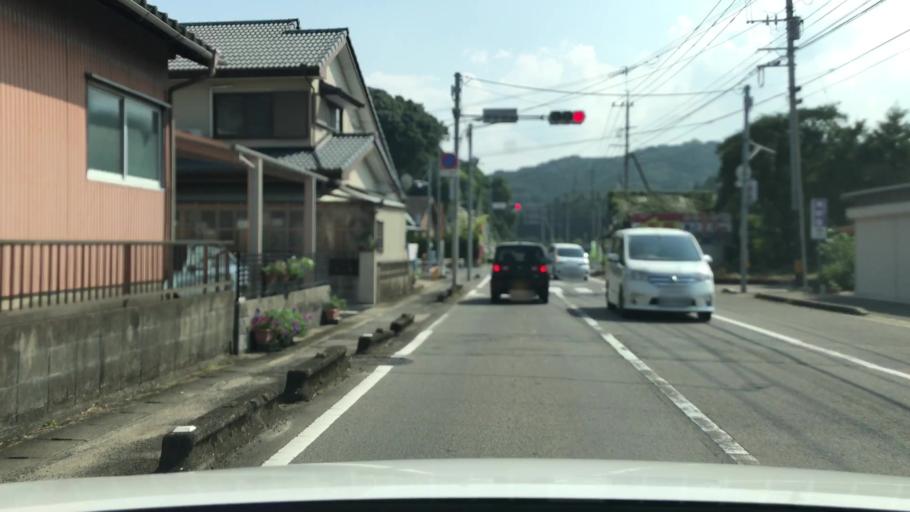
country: JP
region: Saga Prefecture
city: Kashima
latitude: 33.1220
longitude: 130.0638
